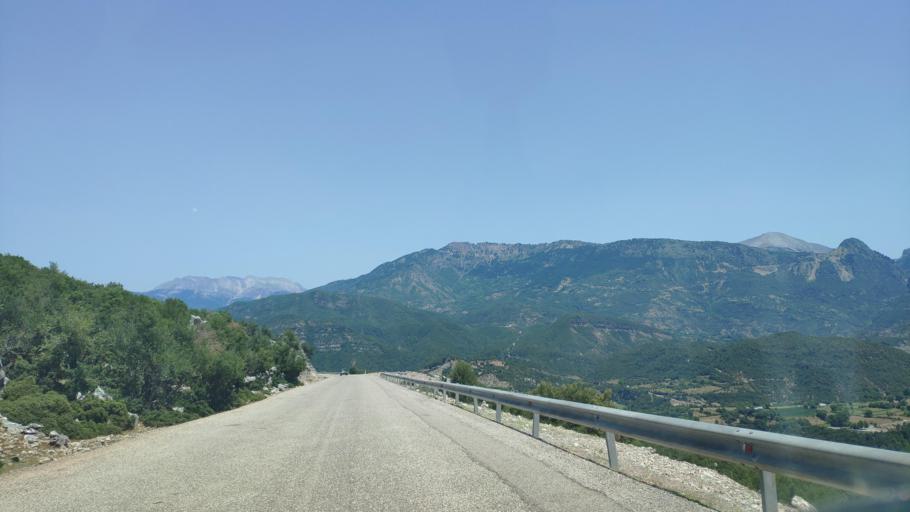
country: GR
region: Thessaly
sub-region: Nomos Kardhitsas
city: Anthiro
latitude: 39.1446
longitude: 21.3870
